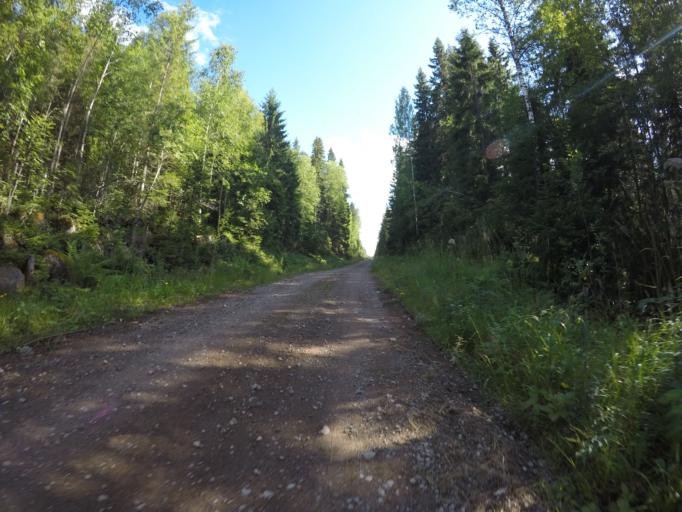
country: SE
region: OErebro
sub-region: Hallefors Kommun
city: Haellefors
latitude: 59.9911
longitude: 14.6074
